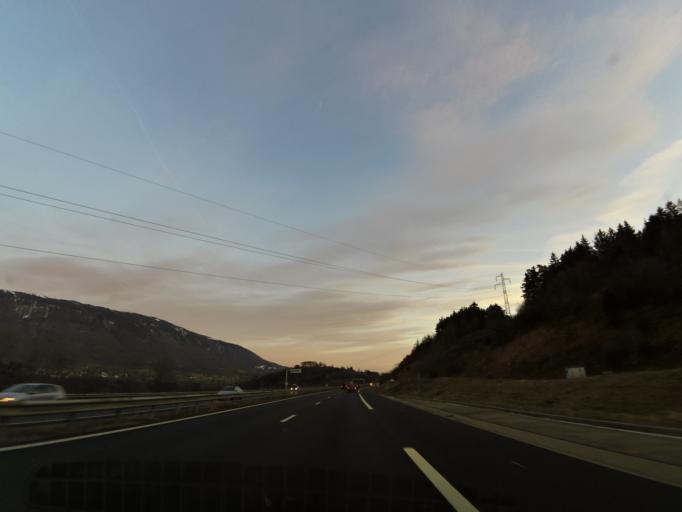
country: FR
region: Rhone-Alpes
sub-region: Departement de l'Ain
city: Chatillon-en-Michaille
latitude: 46.1529
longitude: 5.7881
